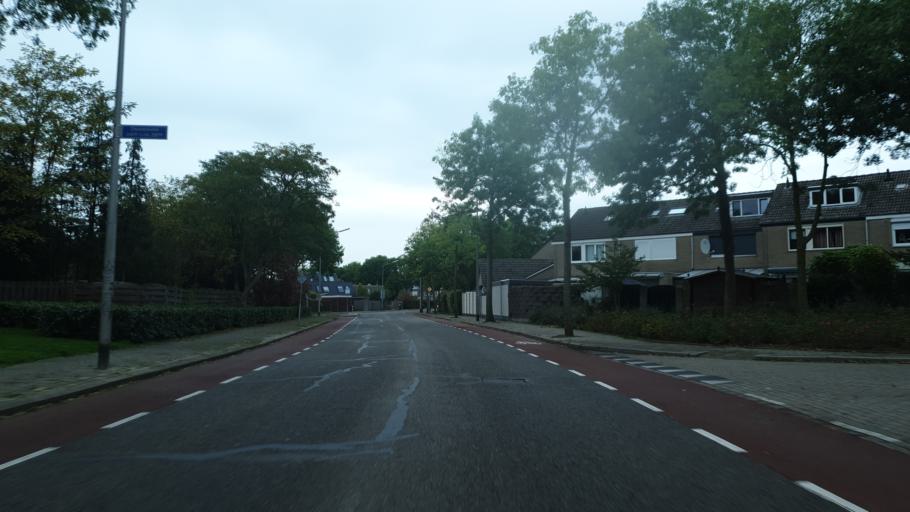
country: NL
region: Gelderland
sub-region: Gemeente Nijmegen
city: Lindenholt
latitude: 51.8194
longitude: 5.8066
